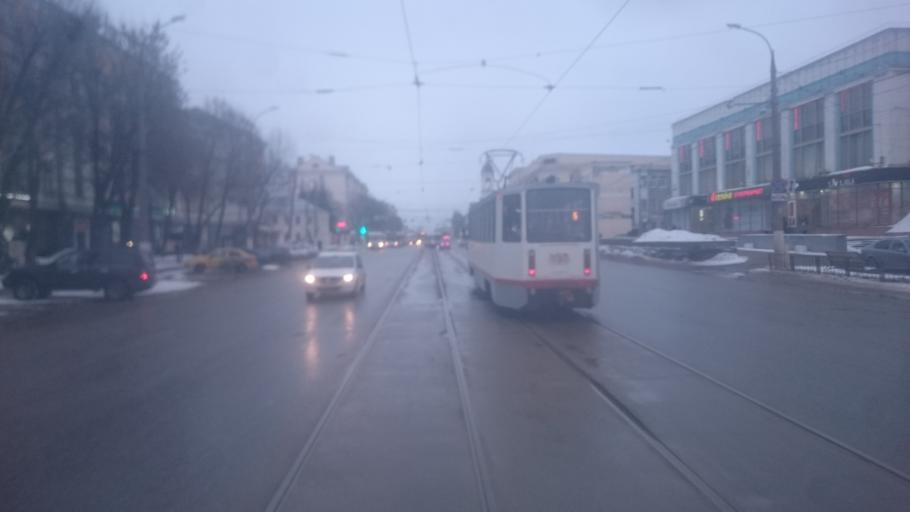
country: RU
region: Tverskaya
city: Tver
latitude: 56.8576
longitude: 35.9078
